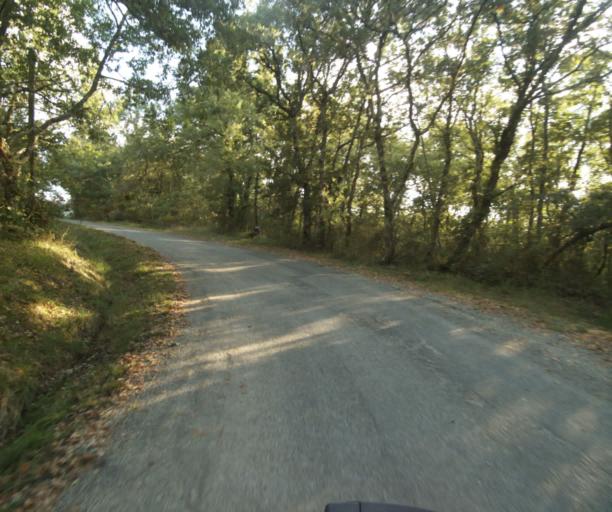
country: FR
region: Midi-Pyrenees
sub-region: Departement de la Haute-Garonne
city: Launac
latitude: 43.8155
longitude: 1.1319
